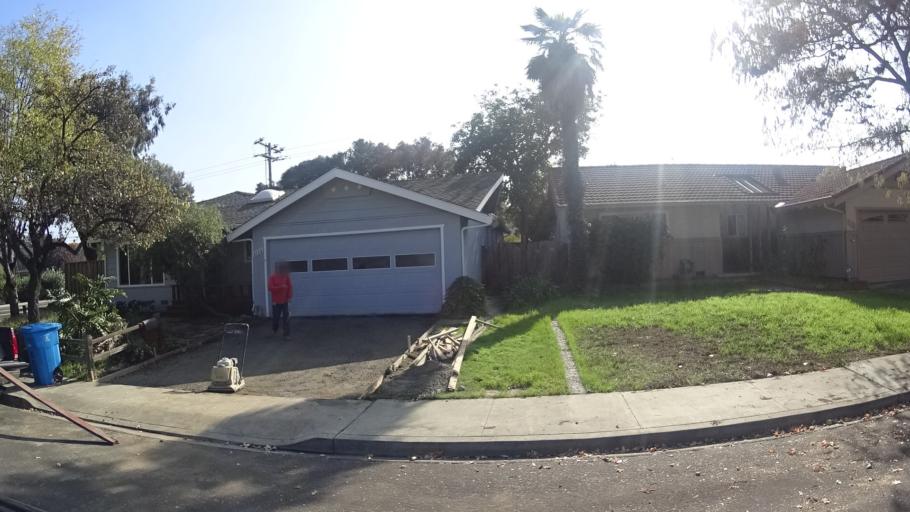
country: US
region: California
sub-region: Santa Clara County
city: Santa Clara
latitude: 37.3550
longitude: -121.9844
